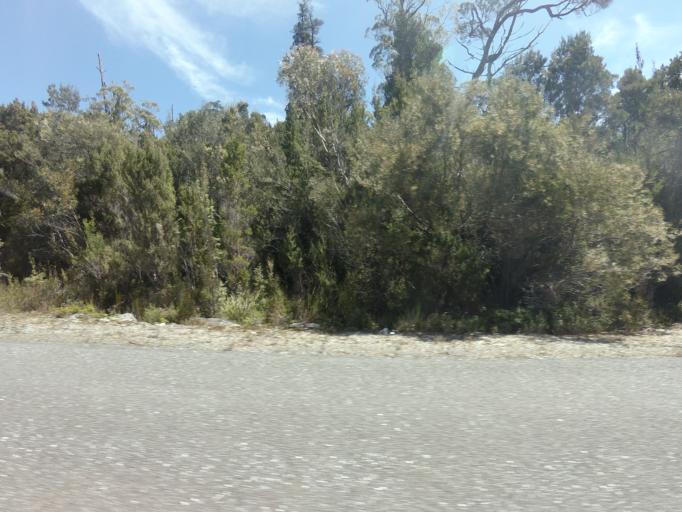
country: AU
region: Tasmania
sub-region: West Coast
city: Queenstown
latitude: -42.7767
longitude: 146.0369
